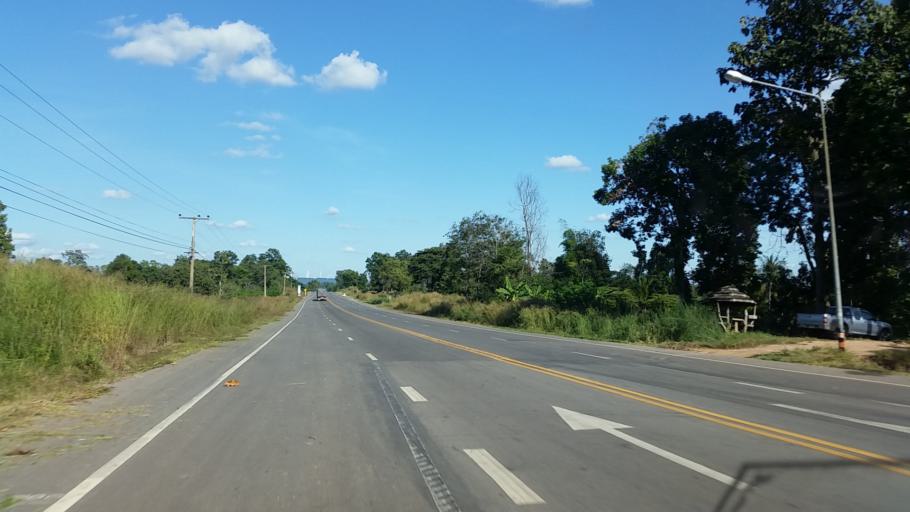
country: TH
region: Chaiyaphum
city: Thep Sathit
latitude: 15.5396
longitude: 101.4327
